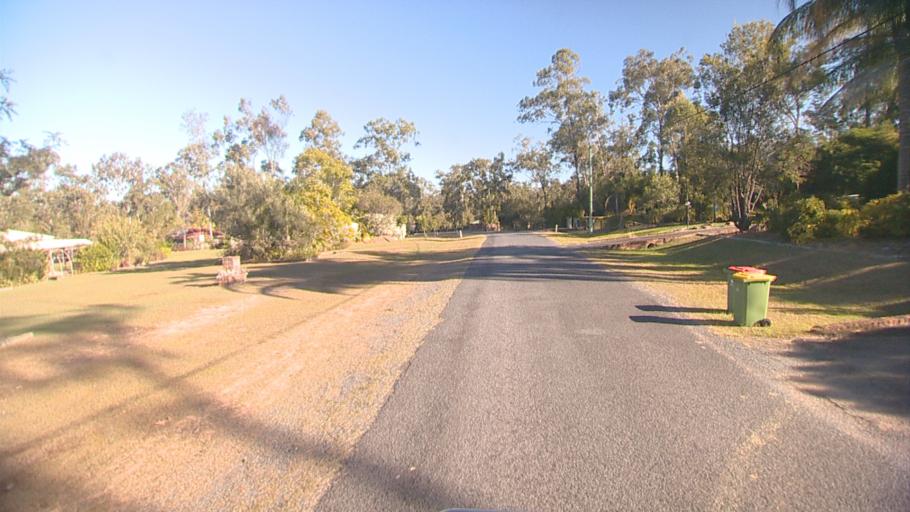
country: AU
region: Queensland
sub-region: Logan
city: North Maclean
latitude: -27.7455
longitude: 153.0195
